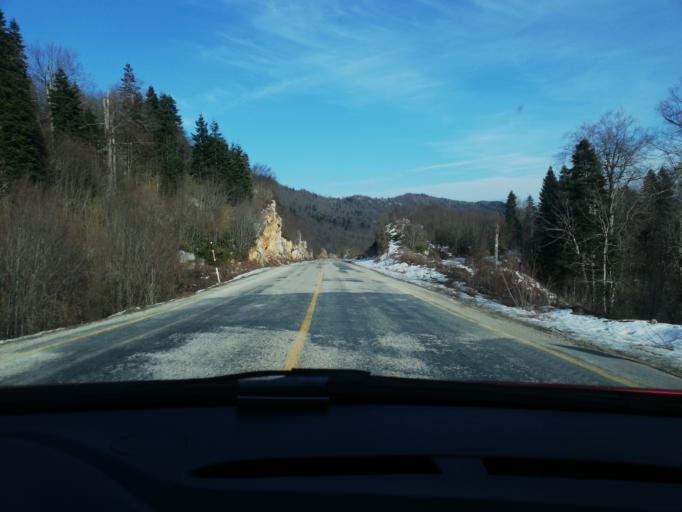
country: TR
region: Kastamonu
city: Cide
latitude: 41.8149
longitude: 33.0944
